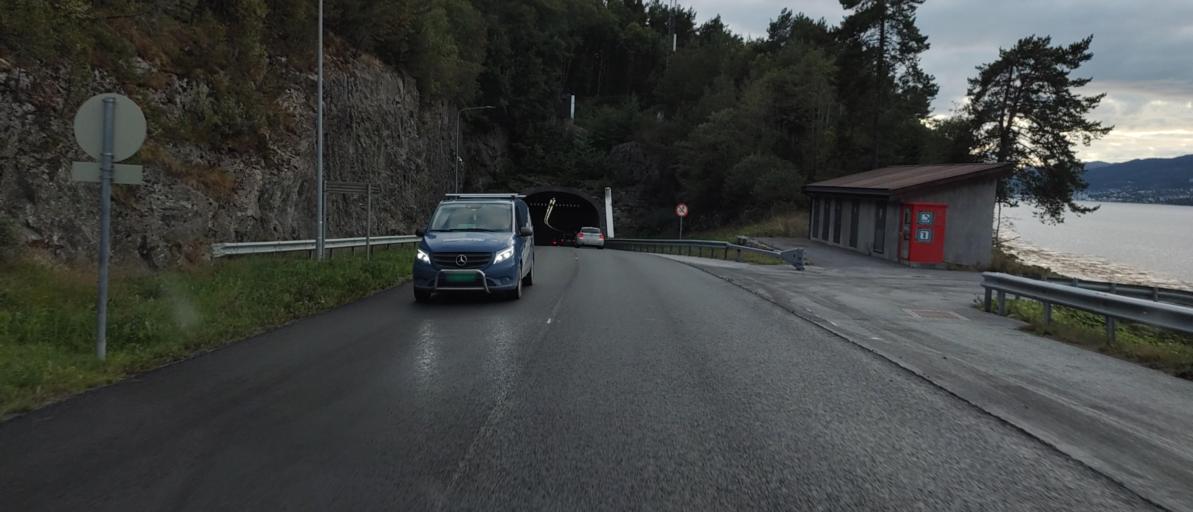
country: NO
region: More og Romsdal
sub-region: Molde
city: Molde
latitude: 62.7347
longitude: 7.2902
